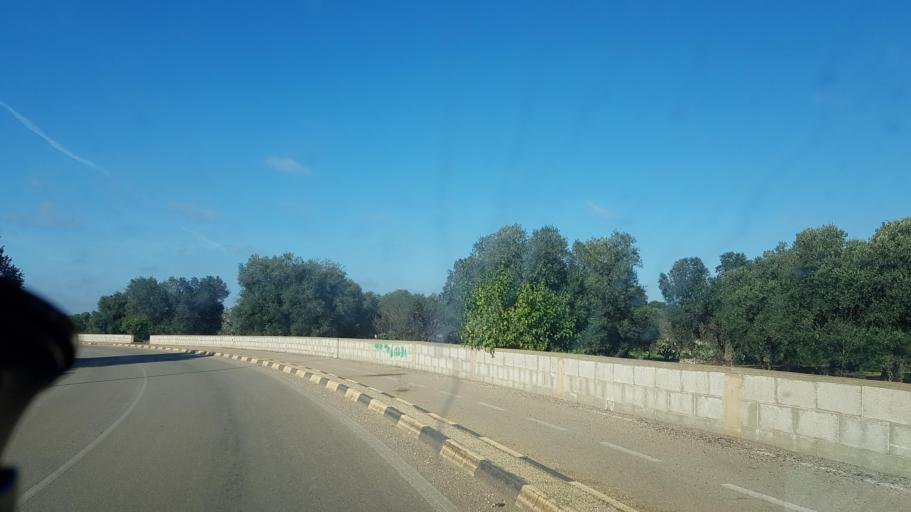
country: IT
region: Apulia
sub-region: Provincia di Brindisi
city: San Vito dei Normanni
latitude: 40.6643
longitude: 17.7139
